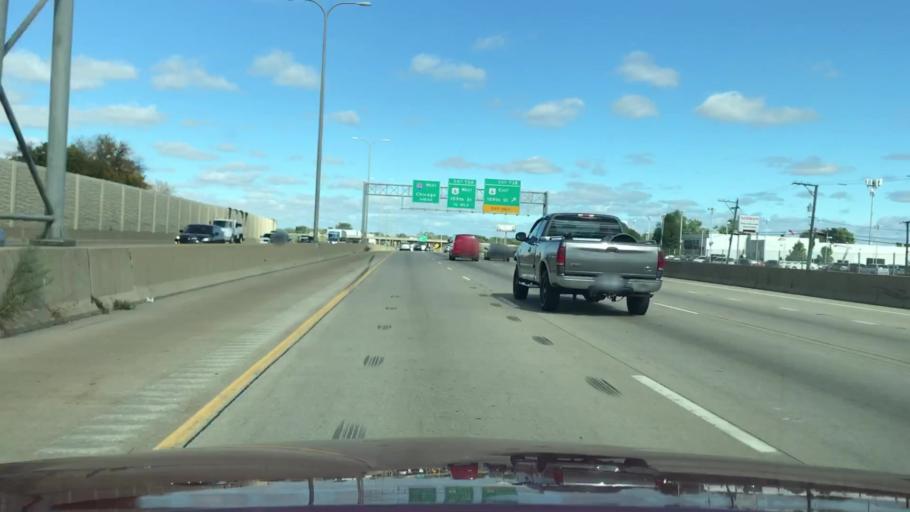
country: US
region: Illinois
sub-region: Cook County
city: South Holland
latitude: 41.5965
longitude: -87.5835
